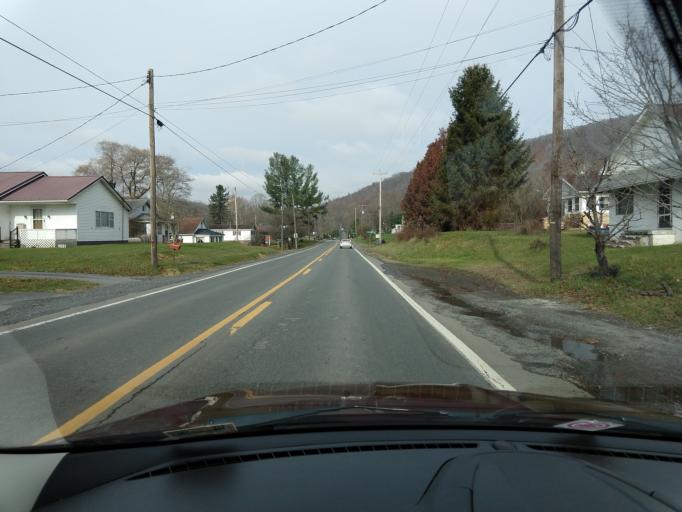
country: US
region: West Virginia
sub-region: Greenbrier County
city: Rainelle
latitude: 37.9816
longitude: -80.7157
